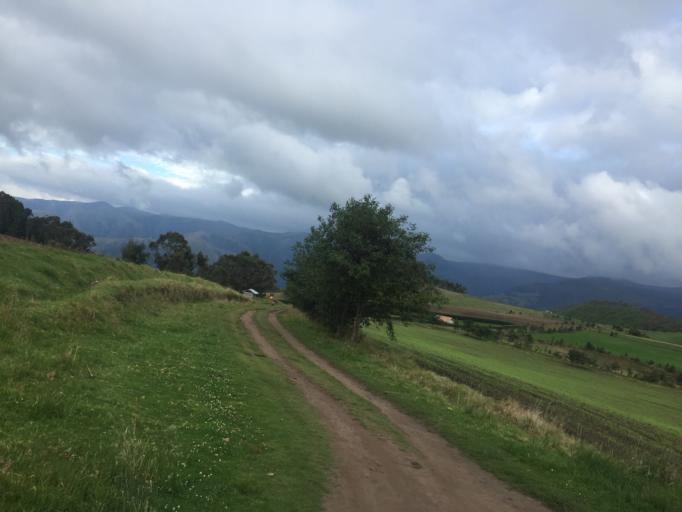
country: EC
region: Imbabura
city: Ibarra
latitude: 0.2259
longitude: -78.1200
